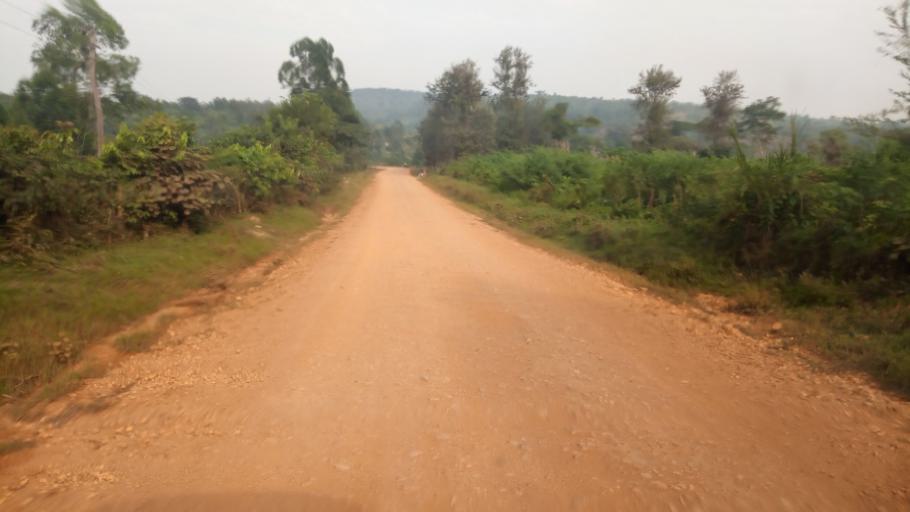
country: UG
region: Western Region
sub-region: Kanungu District
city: Ntungamo
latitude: -0.8387
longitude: 29.6439
